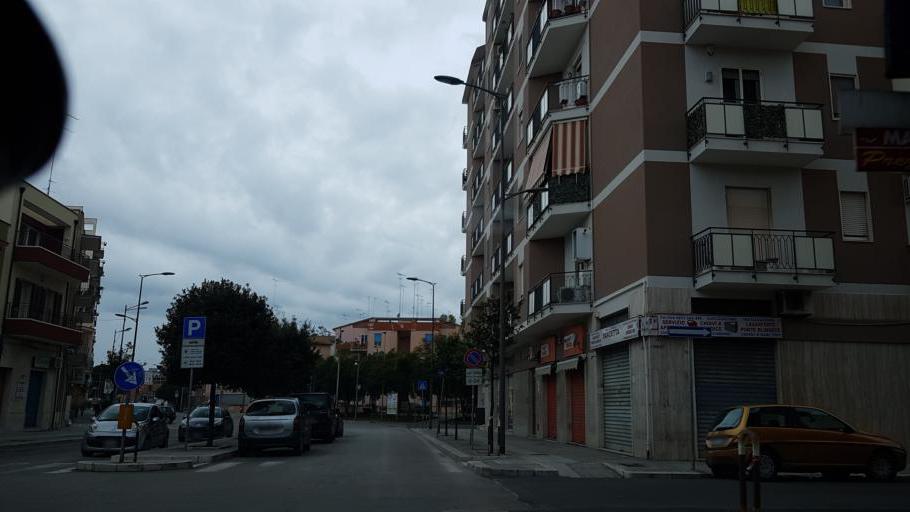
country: IT
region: Apulia
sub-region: Provincia di Brindisi
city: Brindisi
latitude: 40.6296
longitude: 17.9329
